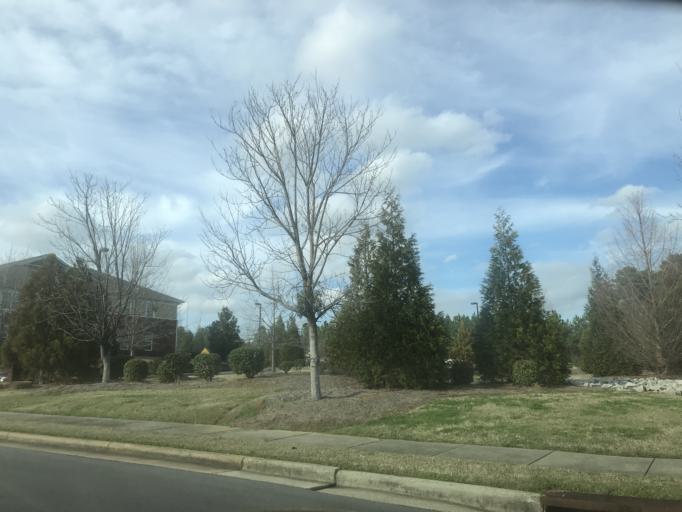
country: US
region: North Carolina
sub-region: Wake County
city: Raleigh
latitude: 35.7669
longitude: -78.6127
